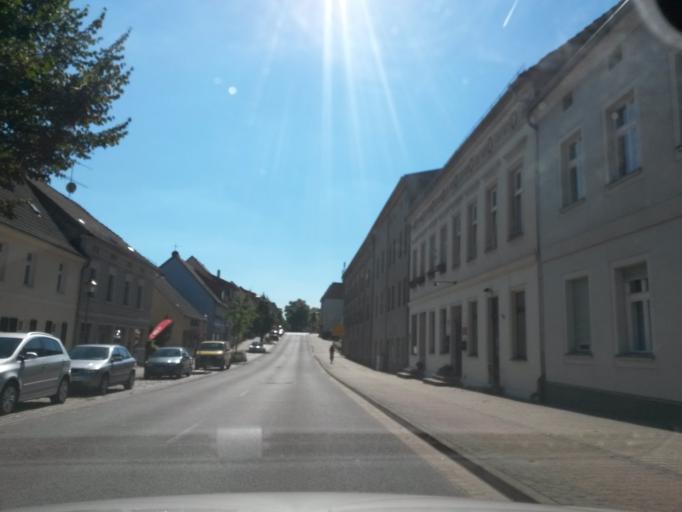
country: DE
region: Brandenburg
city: Lychen
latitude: 53.2121
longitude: 13.3152
